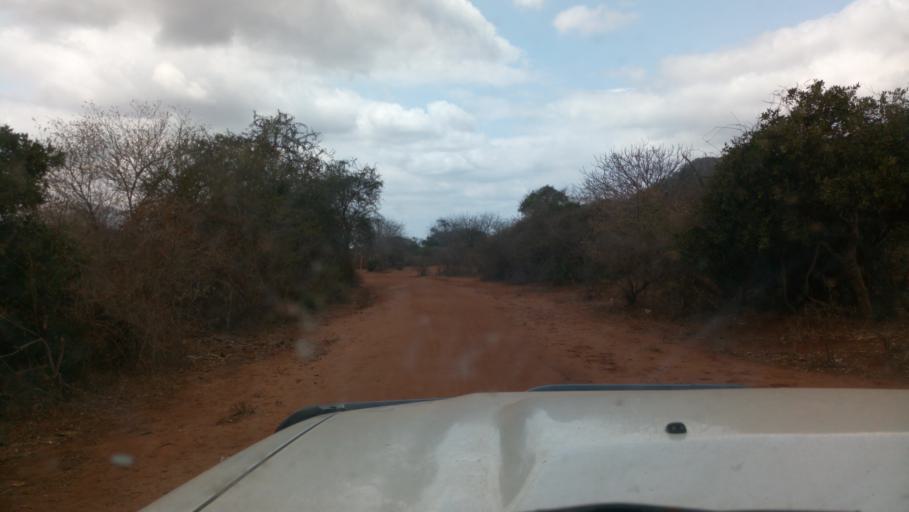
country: KE
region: Kitui
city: Kitui
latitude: -1.8511
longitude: 38.3446
